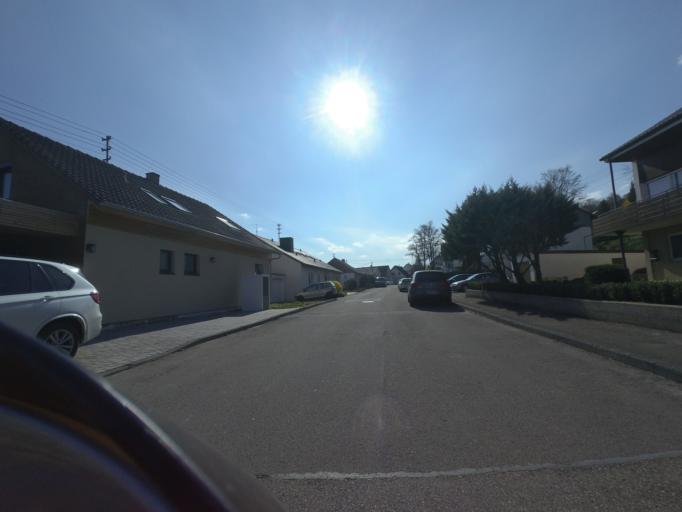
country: DE
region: Baden-Wuerttemberg
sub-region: Regierungsbezirk Stuttgart
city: Unterensingen
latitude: 48.6431
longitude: 9.3459
